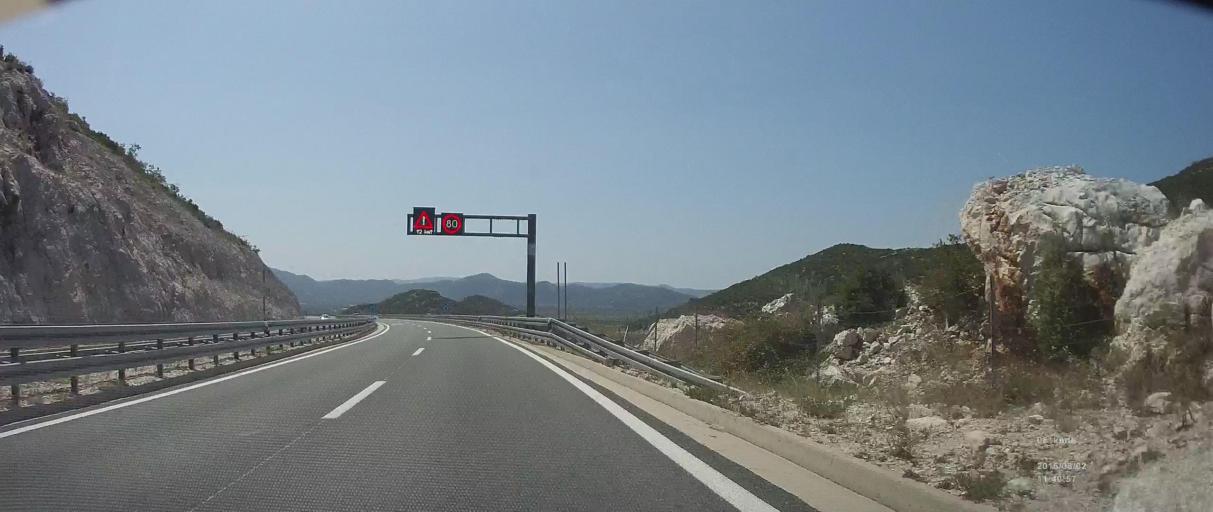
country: HR
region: Dubrovacko-Neretvanska
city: Komin
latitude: 43.0691
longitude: 17.4931
